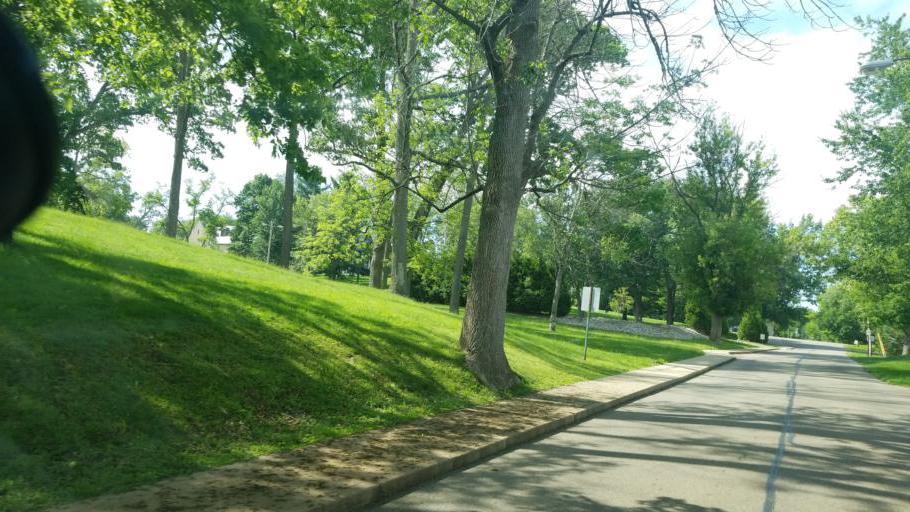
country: US
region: Ohio
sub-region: Knox County
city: Gambier
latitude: 40.3717
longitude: -82.3937
